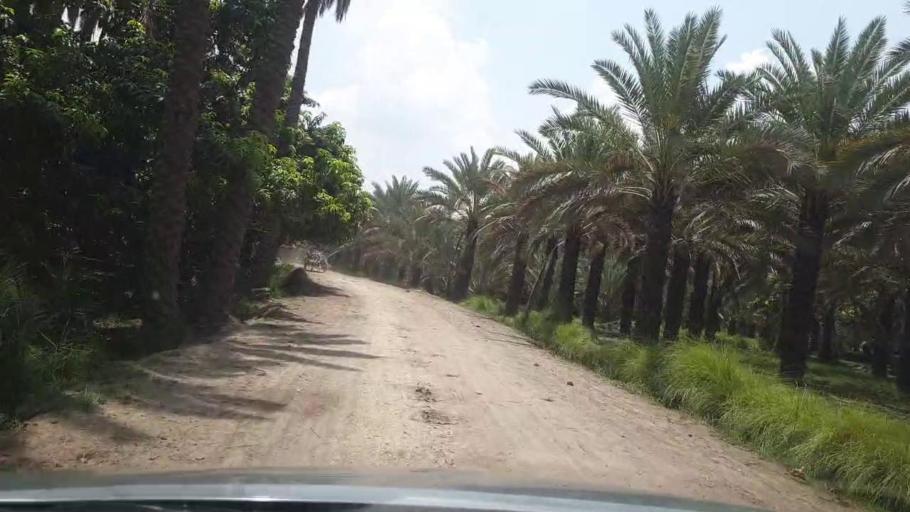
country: PK
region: Sindh
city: Khairpur
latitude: 27.6266
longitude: 68.7428
